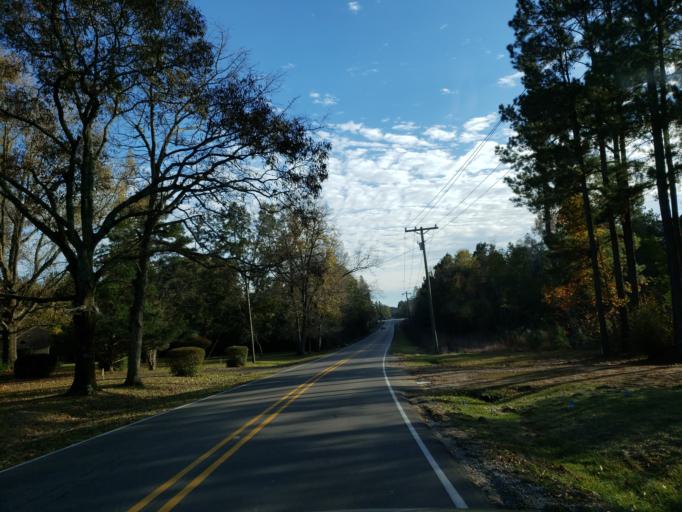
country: US
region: Mississippi
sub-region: Lamar County
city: West Hattiesburg
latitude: 31.3110
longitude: -89.3991
